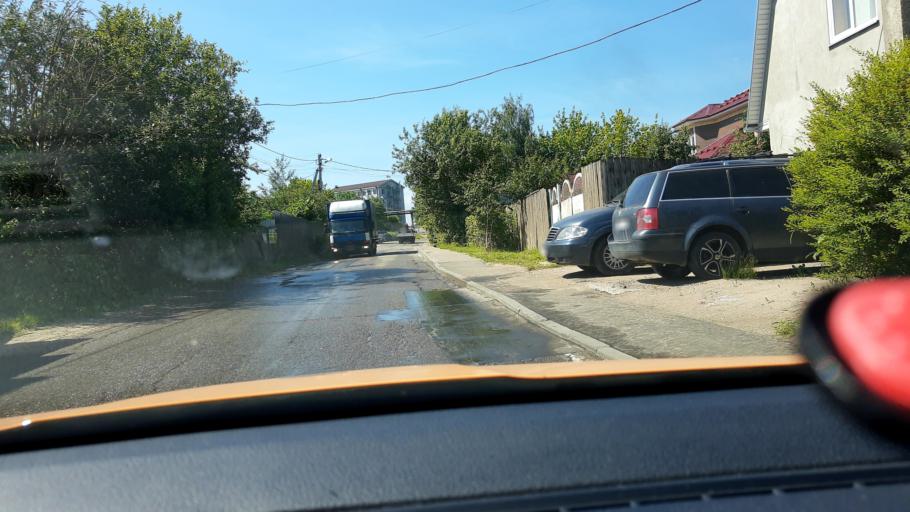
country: RU
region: Moscow
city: Severnyy
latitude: 55.9472
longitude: 37.5314
